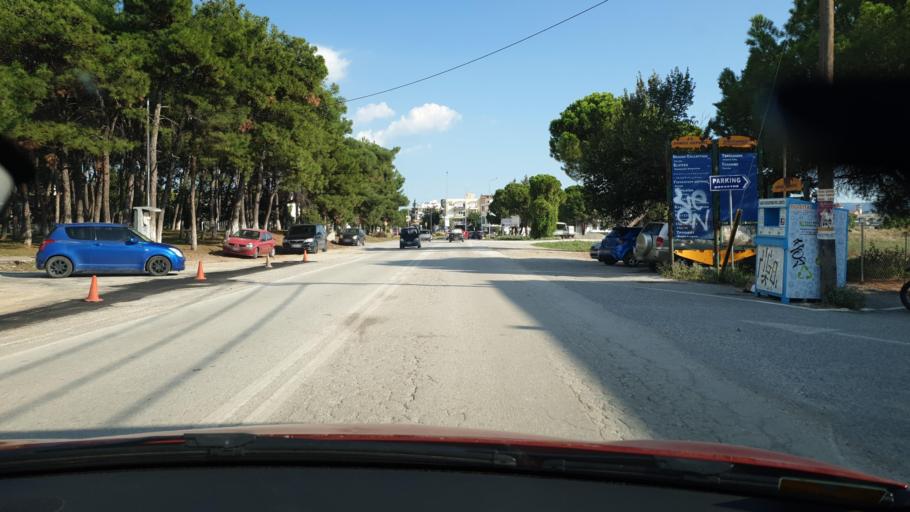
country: GR
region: Central Macedonia
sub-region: Nomos Thessalonikis
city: Thermi
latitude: 40.5539
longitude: 23.0158
